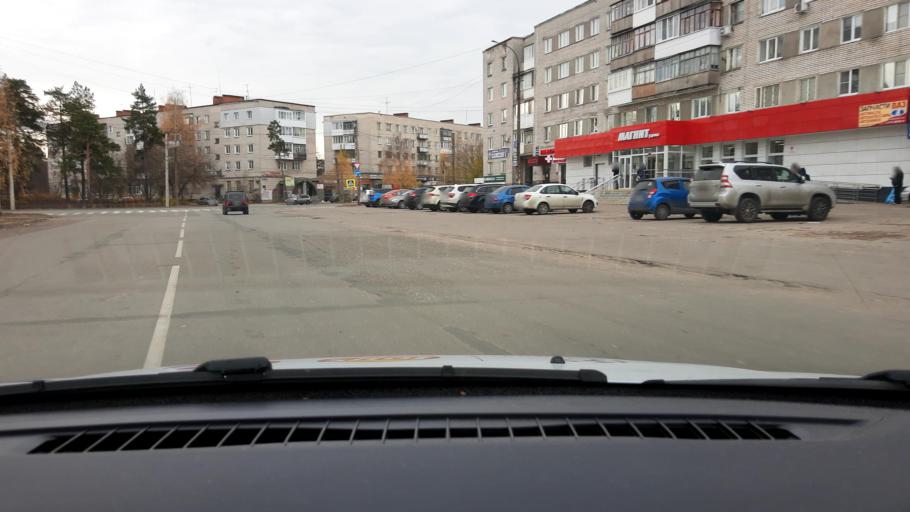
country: RU
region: Nizjnij Novgorod
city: Dzerzhinsk
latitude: 56.2501
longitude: 43.4457
